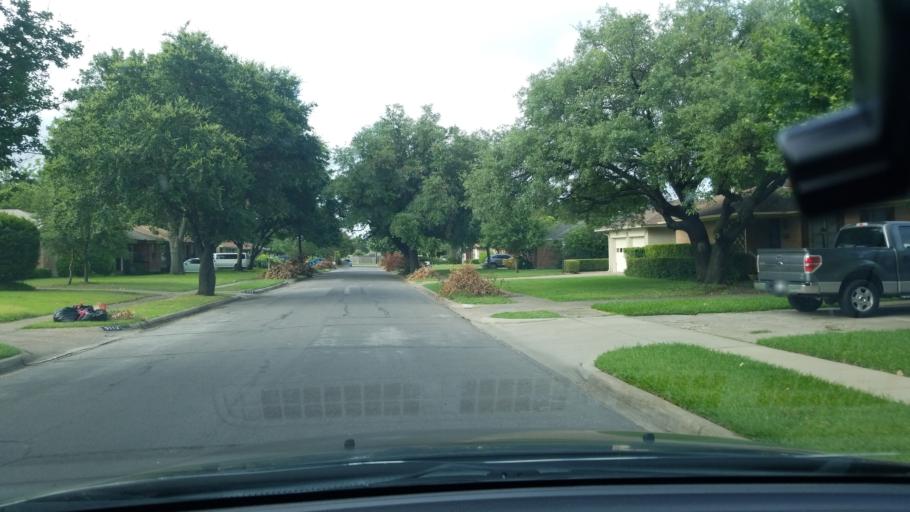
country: US
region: Texas
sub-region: Dallas County
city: Mesquite
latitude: 32.8167
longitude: -96.6797
